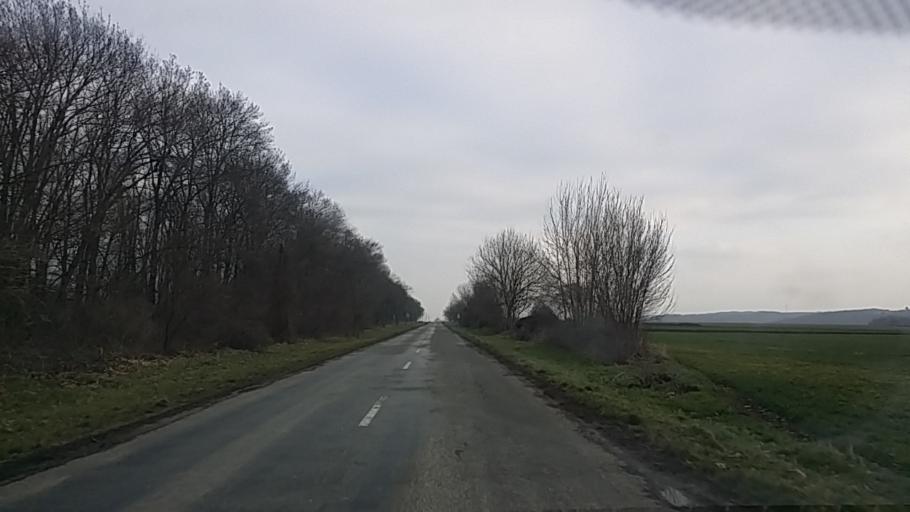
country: HU
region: Baranya
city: Lanycsok
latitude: 46.0953
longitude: 18.5559
